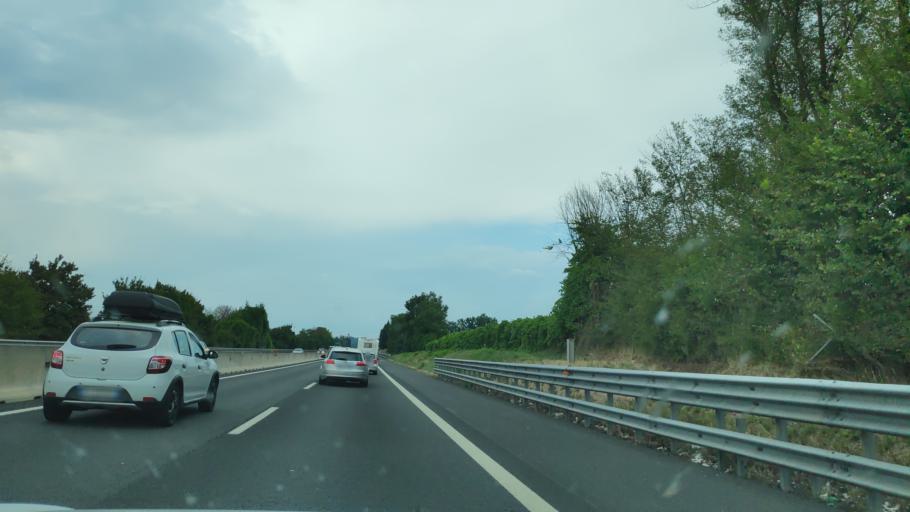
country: IT
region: Tuscany
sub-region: Province of Florence
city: Incisa in Val d'Arno
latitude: 43.6424
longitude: 11.4659
